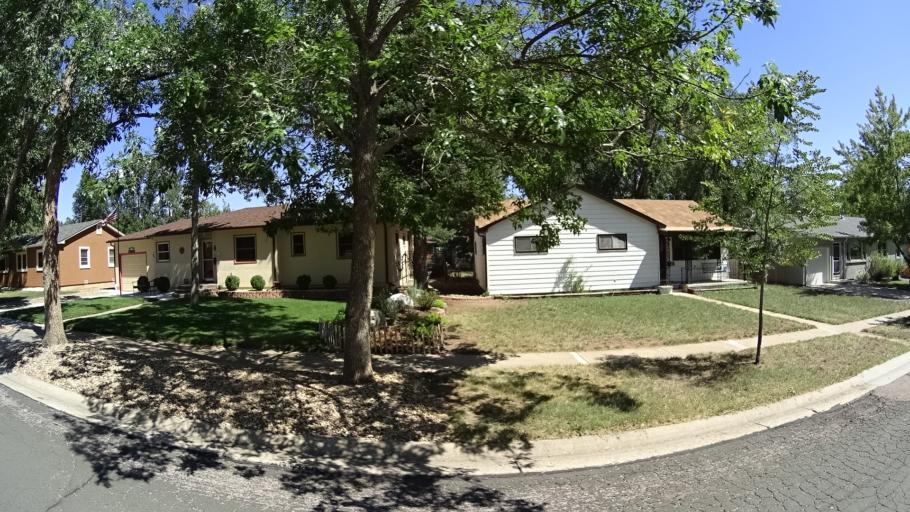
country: US
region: Colorado
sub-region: El Paso County
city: Manitou Springs
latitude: 38.8601
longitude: -104.8706
